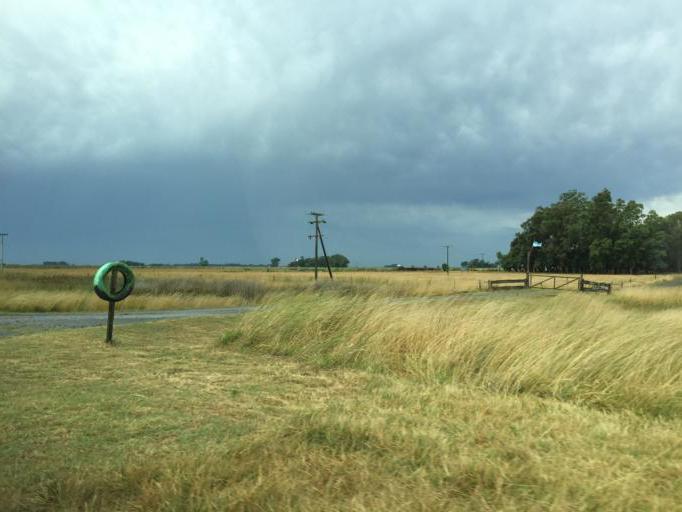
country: AR
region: Buenos Aires
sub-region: Partido de Rauch
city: Rauch
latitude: -36.9614
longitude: -58.9936
